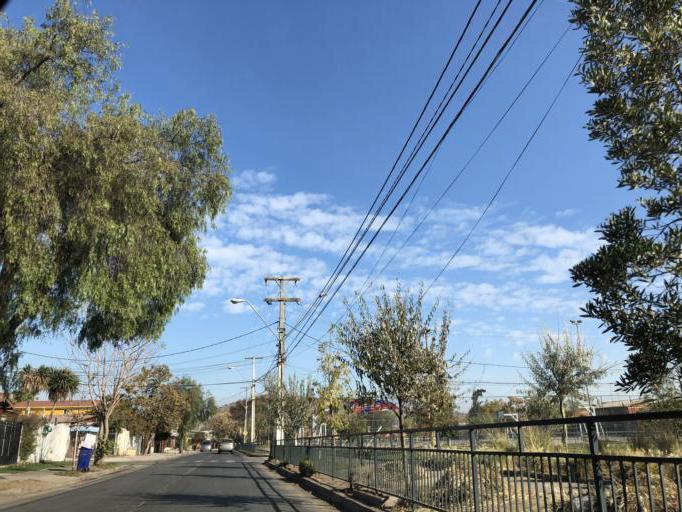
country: CL
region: Santiago Metropolitan
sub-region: Provincia de Cordillera
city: Puente Alto
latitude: -33.6240
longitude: -70.5925
